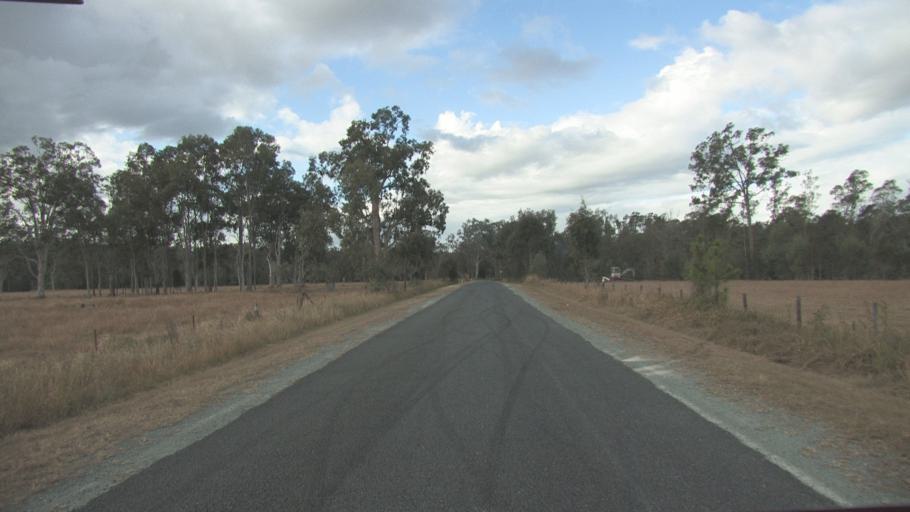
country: AU
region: Queensland
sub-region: Logan
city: Cedar Vale
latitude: -27.8865
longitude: 153.0744
